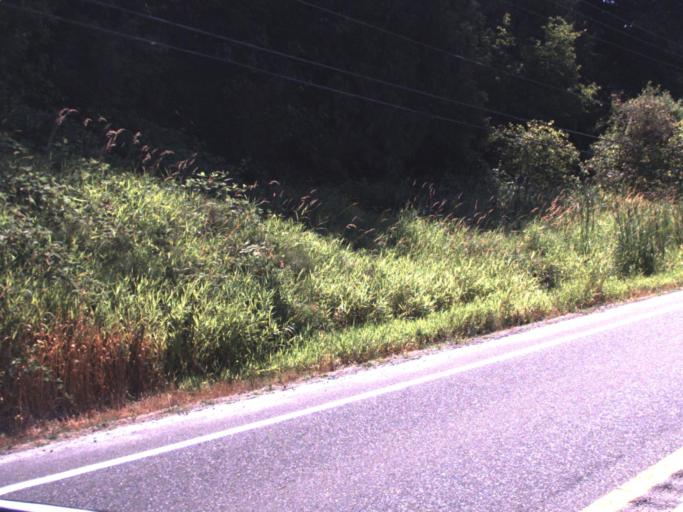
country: US
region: Washington
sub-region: King County
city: Ames Lake
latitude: 47.6025
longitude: -121.9614
